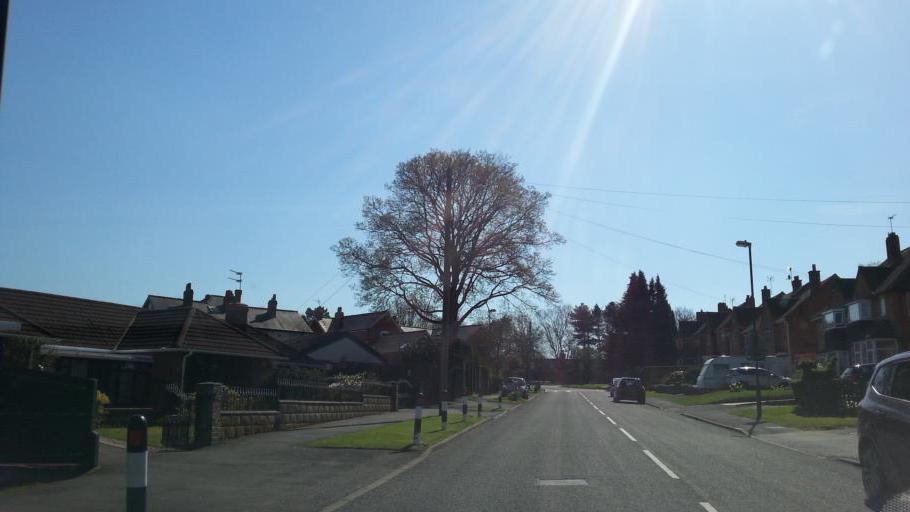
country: GB
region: England
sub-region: Worcestershire
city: Barnt Green
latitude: 52.3910
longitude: -2.0303
